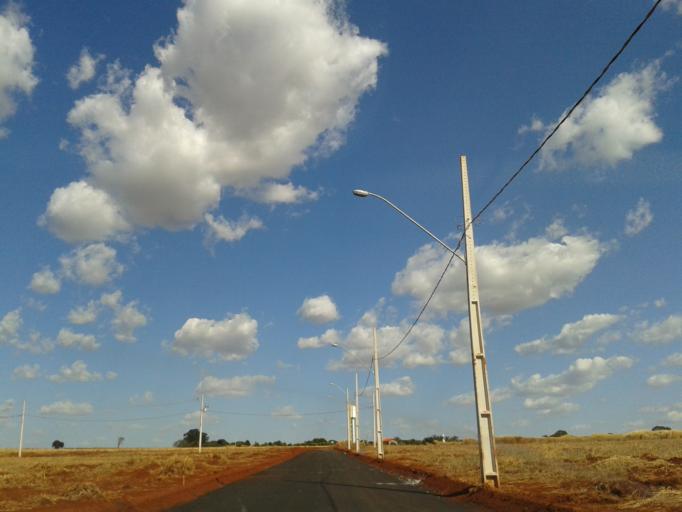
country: BR
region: Minas Gerais
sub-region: Capinopolis
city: Capinopolis
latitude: -18.6939
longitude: -49.5770
